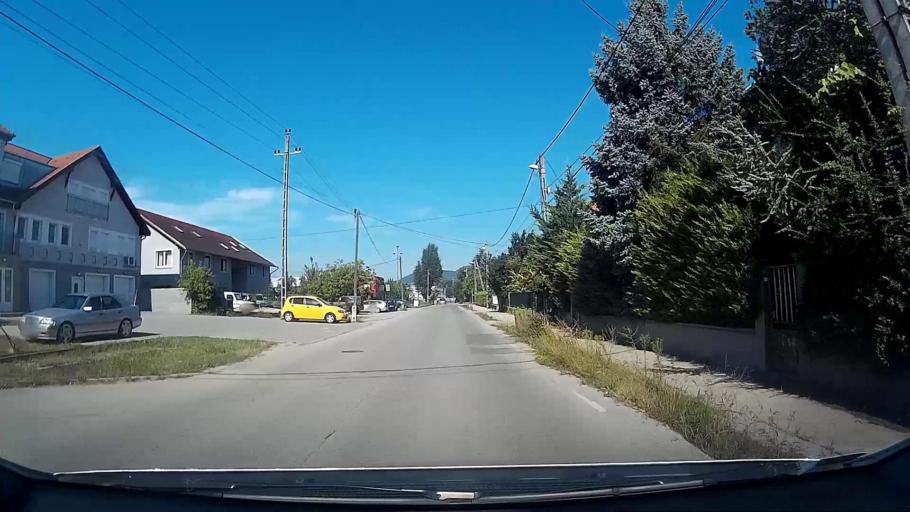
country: HU
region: Pest
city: Szentendre
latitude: 47.6621
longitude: 19.0656
